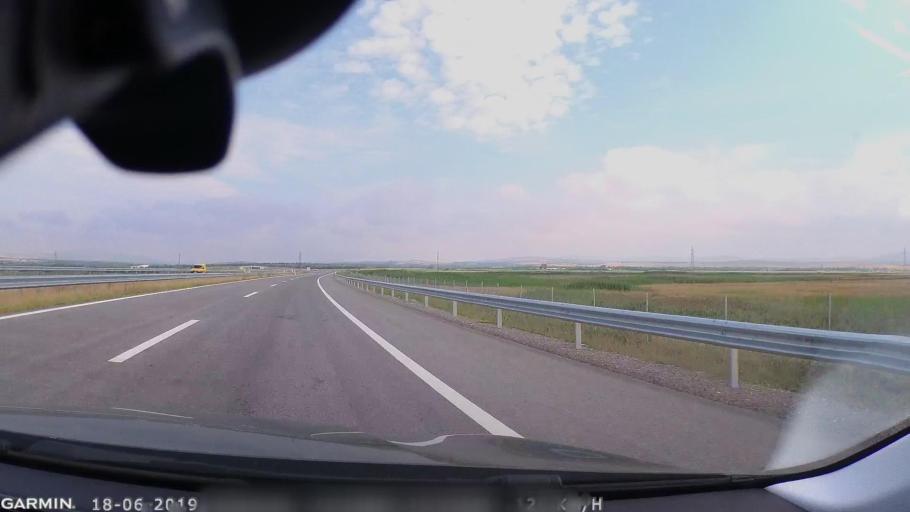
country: MK
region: Sveti Nikole
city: Sveti Nikole
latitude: 41.8181
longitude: 22.0163
